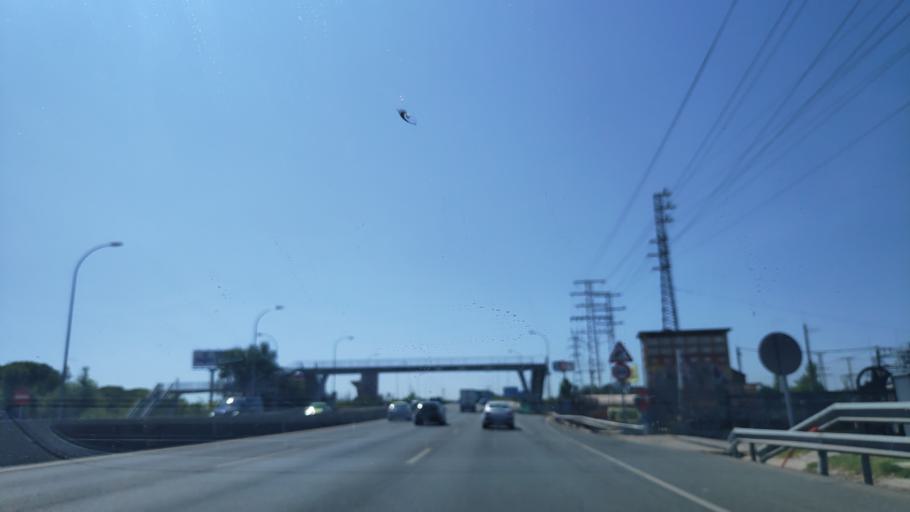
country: ES
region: Madrid
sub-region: Provincia de Madrid
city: Villaverde
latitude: 40.3454
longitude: -3.7236
